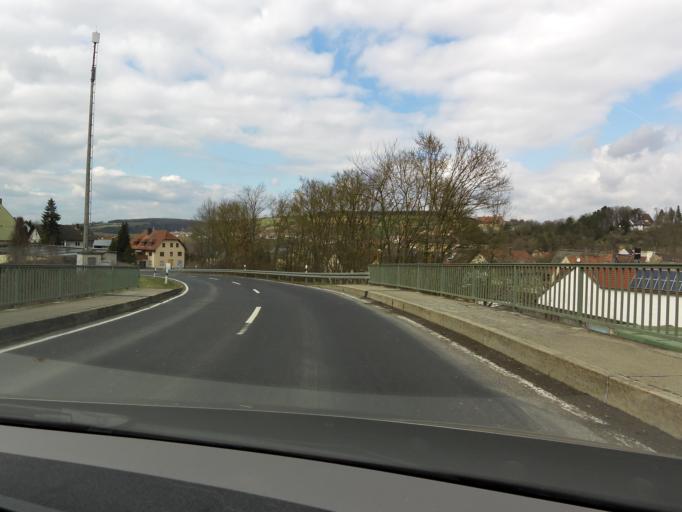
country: DE
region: Bavaria
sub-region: Regierungsbezirk Unterfranken
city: Arnstein
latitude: 49.9739
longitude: 9.9743
